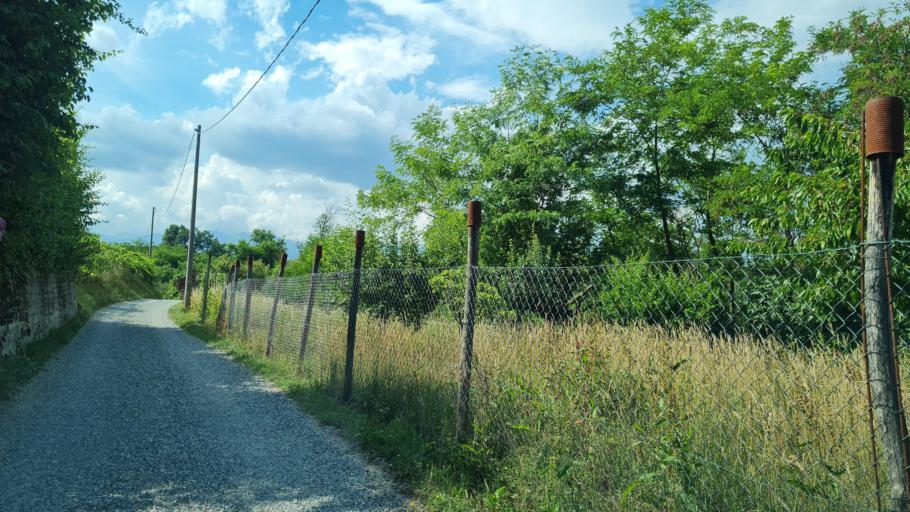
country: IT
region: Piedmont
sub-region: Provincia di Biella
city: Masserano
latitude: 45.5781
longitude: 8.2155
